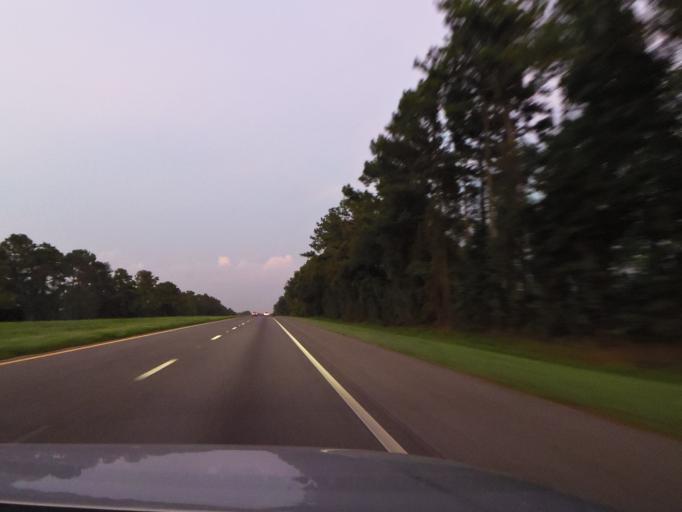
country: US
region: Florida
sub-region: Madison County
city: Madison
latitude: 30.4324
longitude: -83.5405
